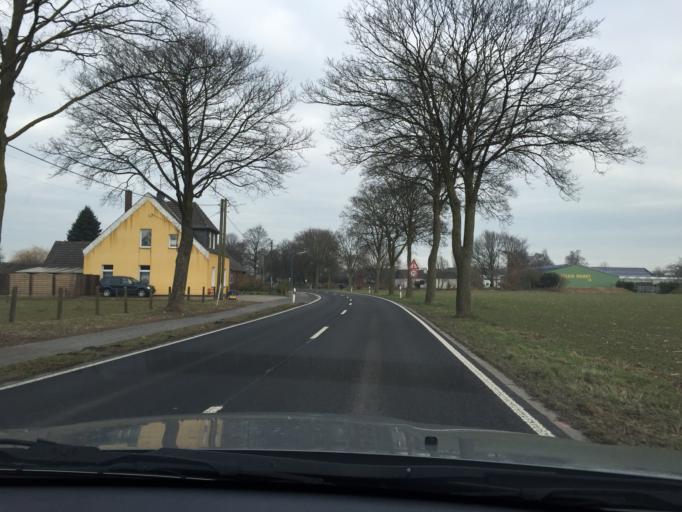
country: DE
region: North Rhine-Westphalia
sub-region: Regierungsbezirk Dusseldorf
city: Kleve
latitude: 51.7654
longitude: 6.1324
